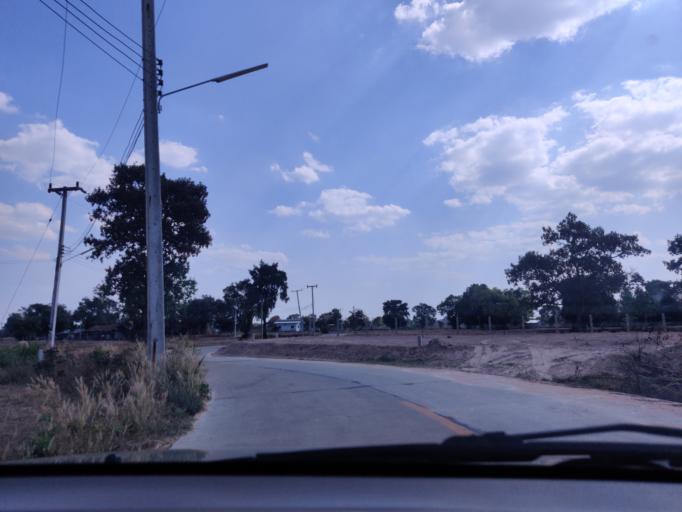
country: TH
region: Sisaket
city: Si Sa Ket
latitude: 15.0885
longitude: 104.3529
